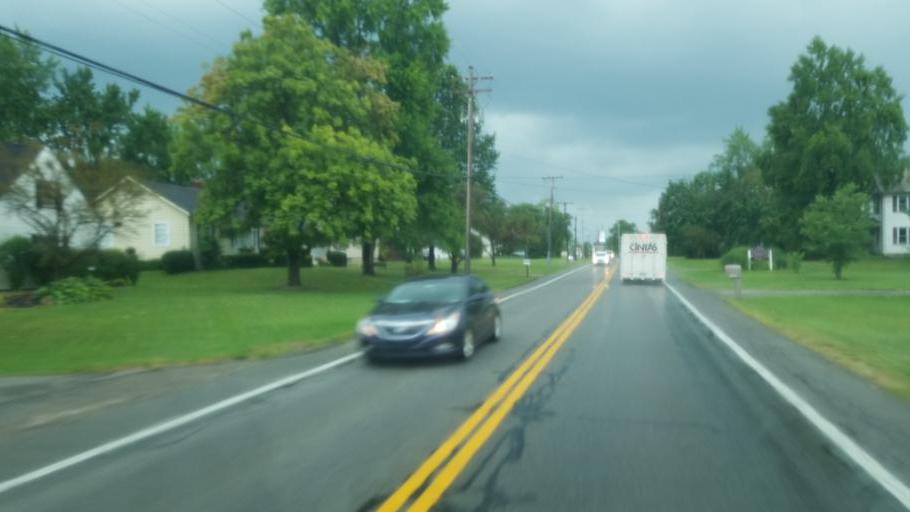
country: US
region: Ohio
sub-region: Trumbull County
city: Champion Heights
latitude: 41.2952
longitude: -80.8485
